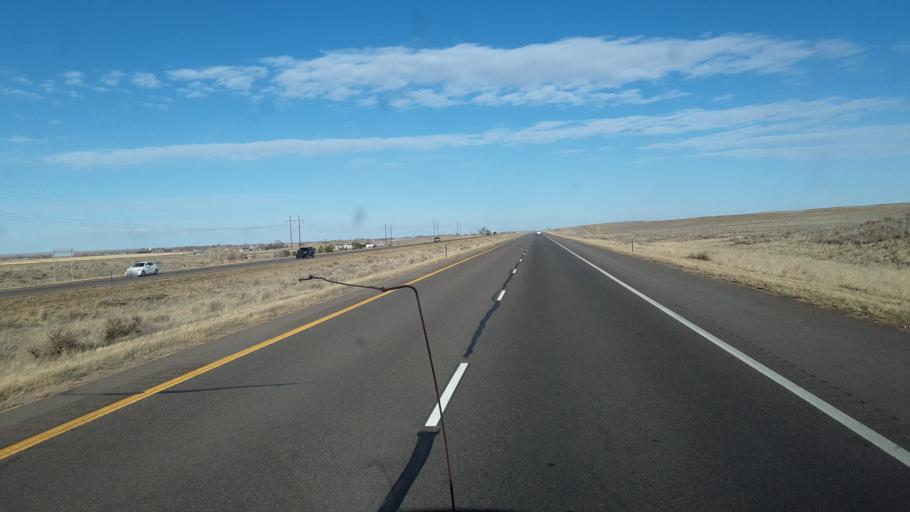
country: US
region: Colorado
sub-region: Morgan County
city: Brush
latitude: 40.2931
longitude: -103.5413
